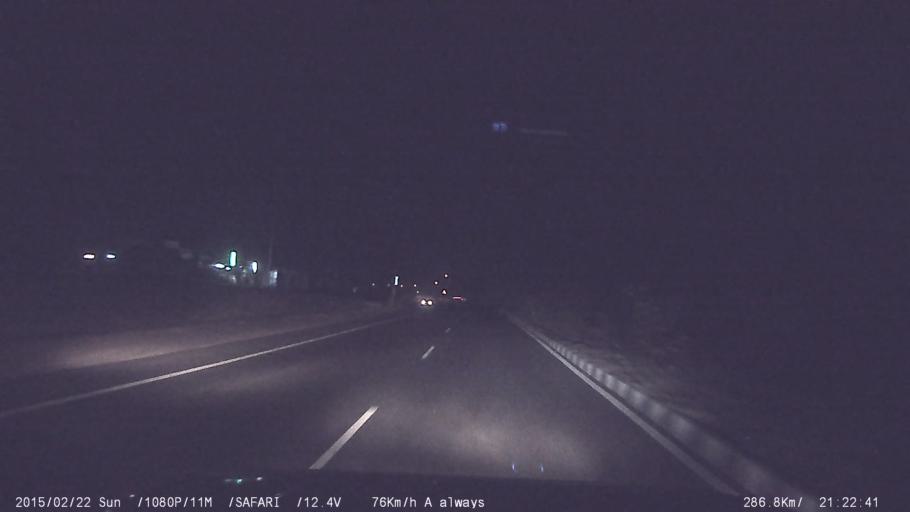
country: IN
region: Tamil Nadu
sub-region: Karur
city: Karur
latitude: 10.8746
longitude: 78.0029
